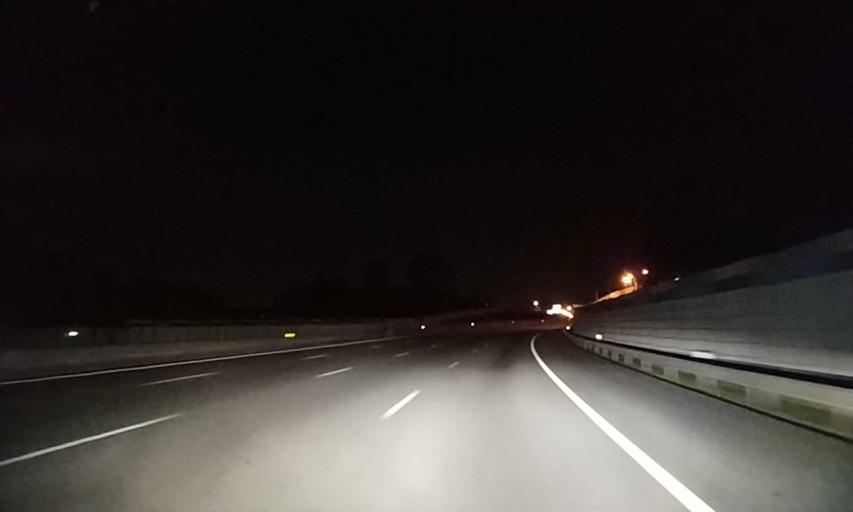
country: PT
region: Porto
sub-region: Vila Nova de Gaia
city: Grijo
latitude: 41.0339
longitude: -8.5716
